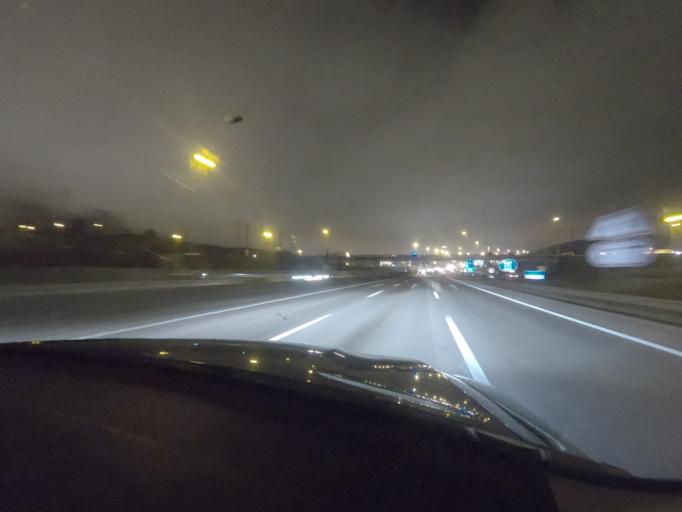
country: PT
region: Lisbon
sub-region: Vila Franca de Xira
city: Vialonga
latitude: 38.8926
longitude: -9.0496
